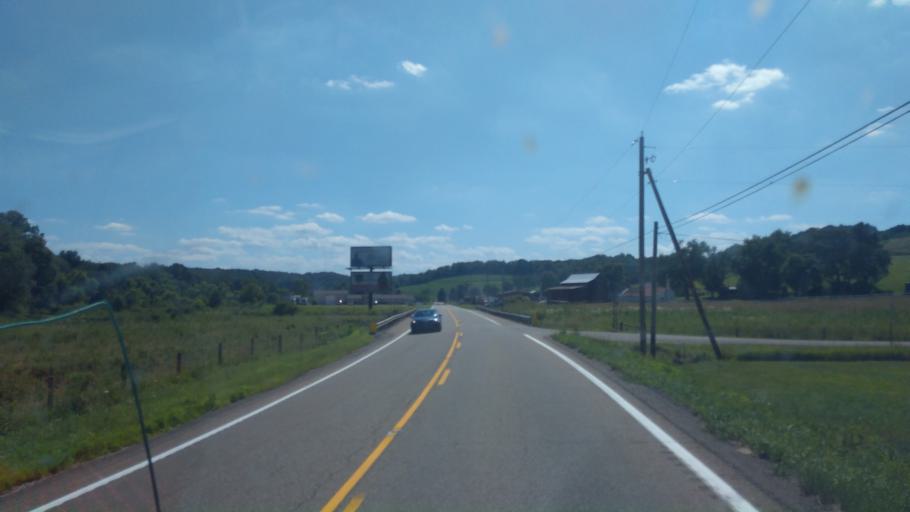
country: US
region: Ohio
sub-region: Carroll County
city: Carrollton
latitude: 40.5752
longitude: -81.1204
